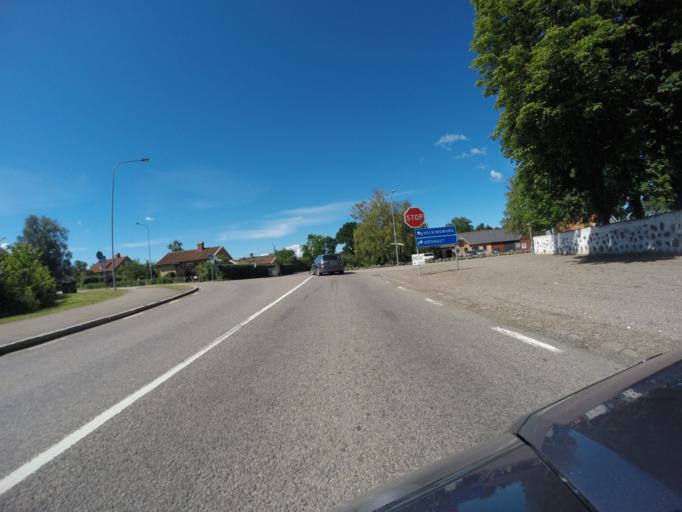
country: SE
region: Skane
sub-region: Helsingborg
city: Odakra
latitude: 56.1086
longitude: 12.6920
